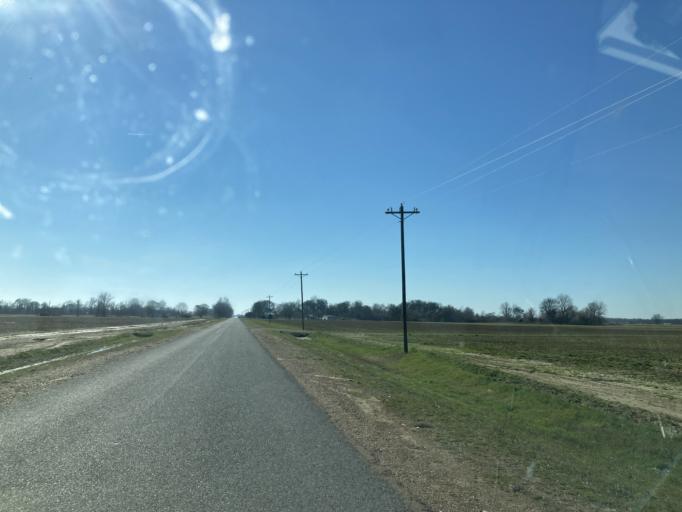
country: US
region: Mississippi
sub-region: Yazoo County
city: Yazoo City
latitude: 32.9743
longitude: -90.5943
